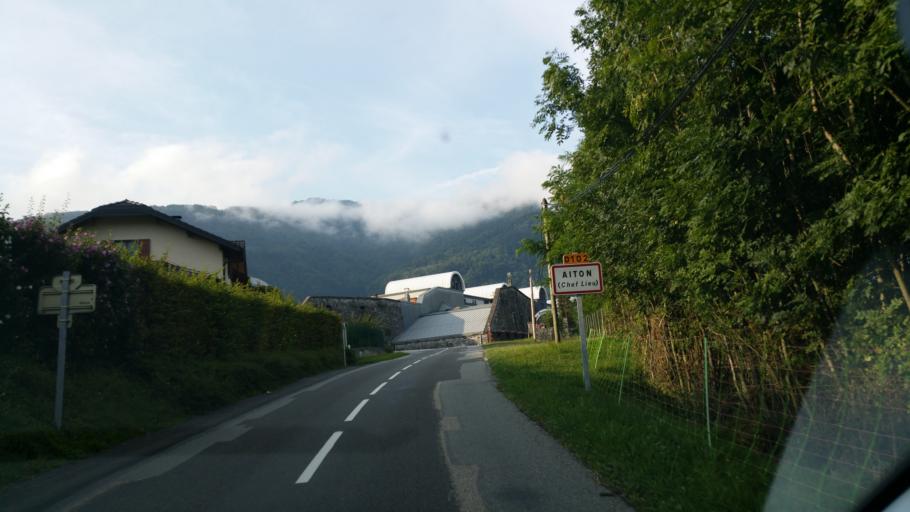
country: FR
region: Rhone-Alpes
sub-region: Departement de la Savoie
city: Aiton
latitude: 45.5609
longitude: 6.2548
